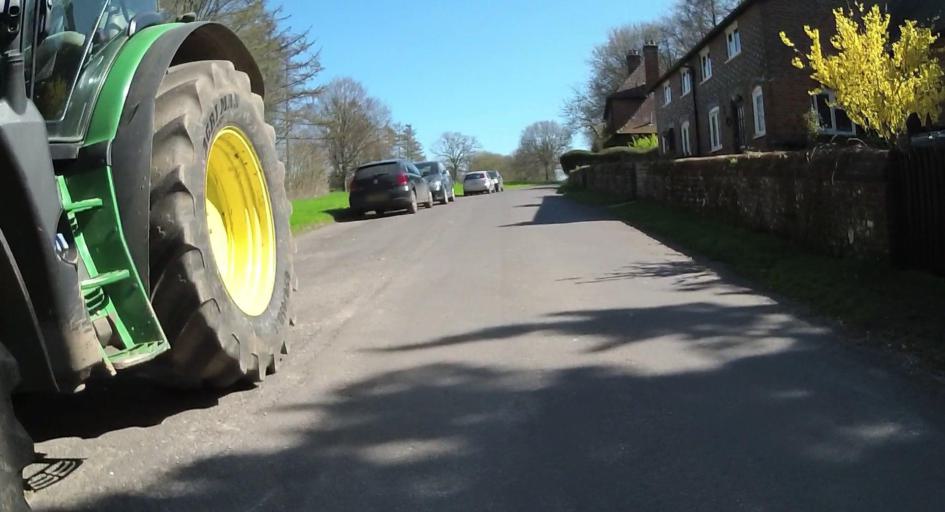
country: GB
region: England
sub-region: Hampshire
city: Kingsclere
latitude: 51.2714
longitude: -1.1920
